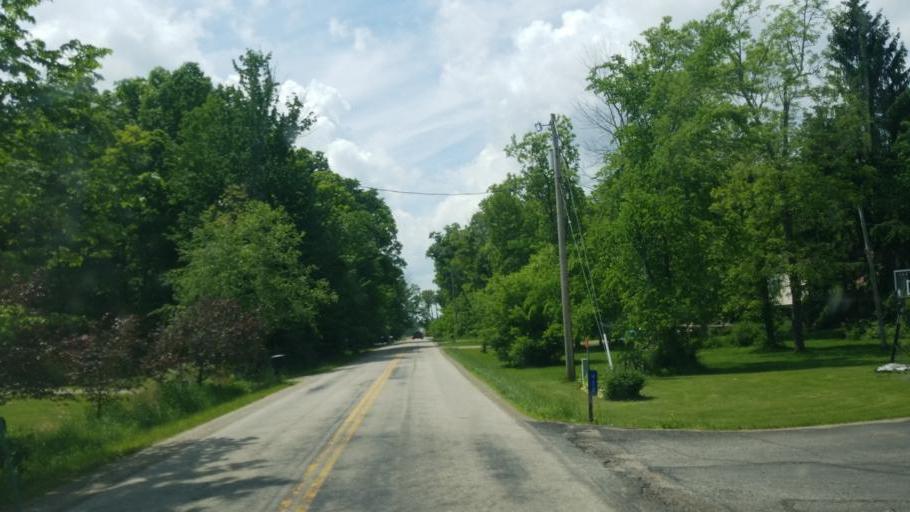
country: US
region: Ohio
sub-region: Ashland County
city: Ashland
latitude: 40.8060
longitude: -82.3012
